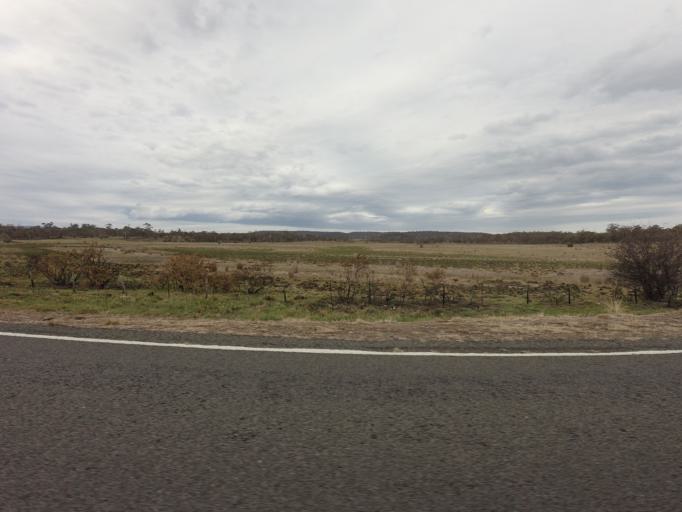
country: AU
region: Tasmania
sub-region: Break O'Day
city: St Helens
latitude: -42.0453
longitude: 148.0523
